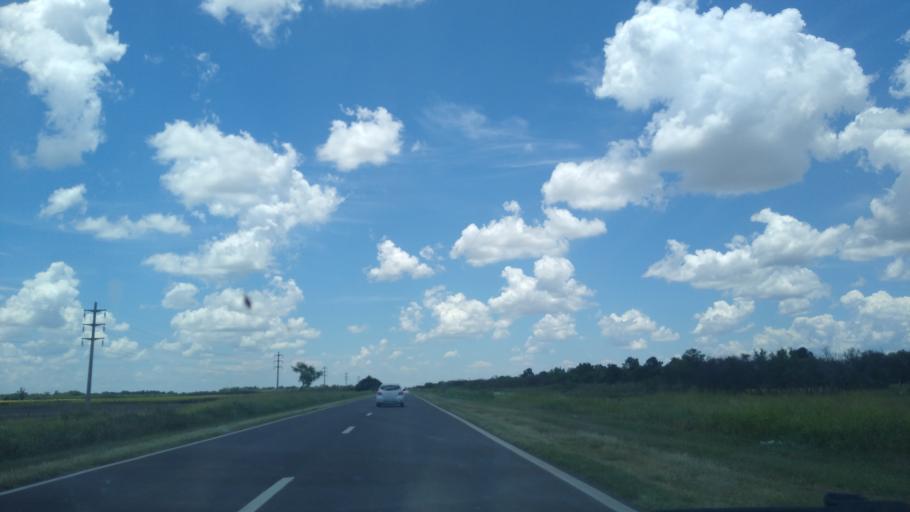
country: AR
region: Chaco
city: Presidencia Roque Saenz Pena
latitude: -26.7388
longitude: -60.3861
